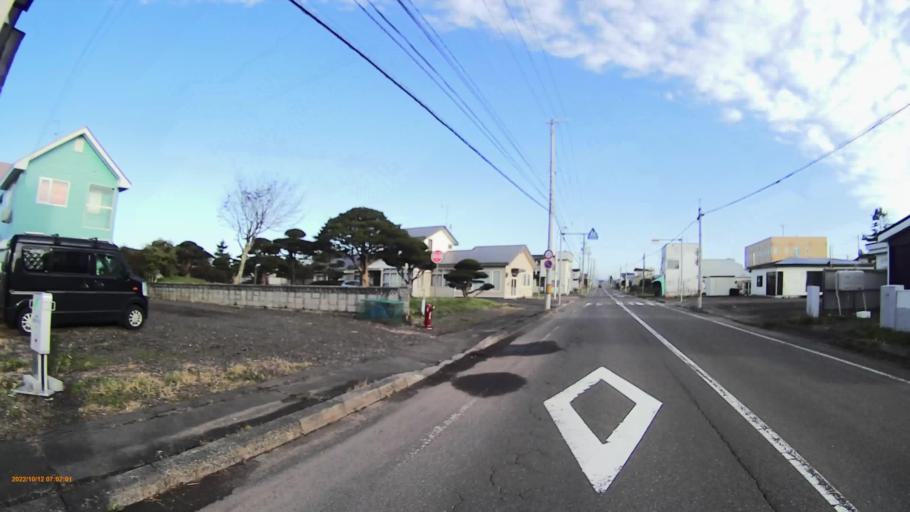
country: JP
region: Hokkaido
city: Kushiro
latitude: 42.8917
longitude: 143.9324
